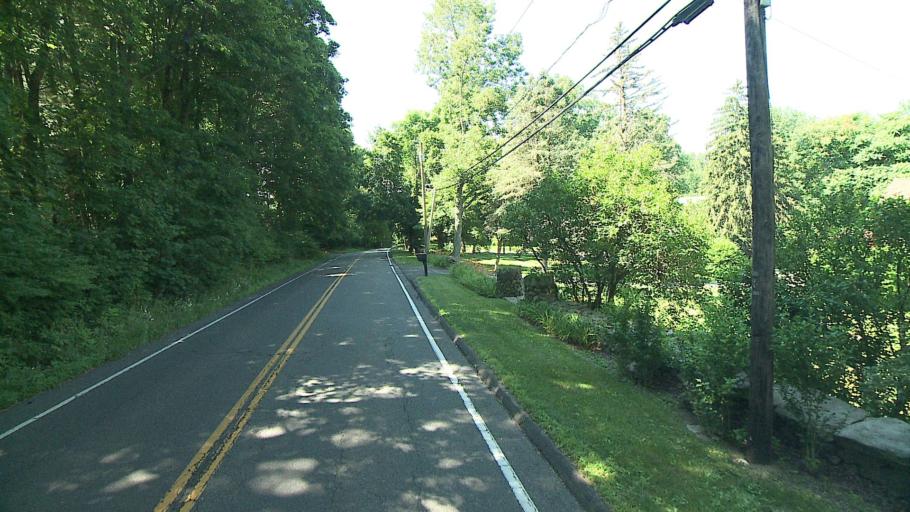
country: US
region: Connecticut
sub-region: Fairfield County
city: Ridgefield
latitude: 41.2588
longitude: -73.5153
